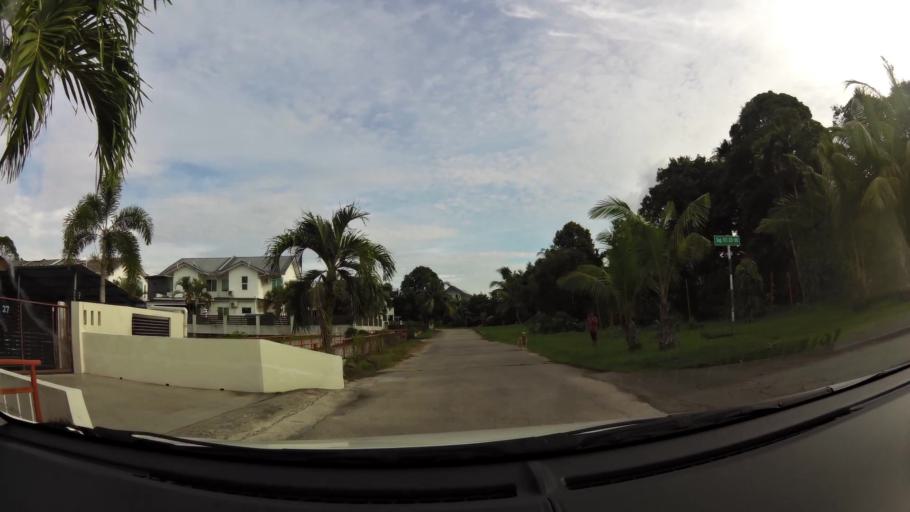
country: BN
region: Brunei and Muara
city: Bandar Seri Begawan
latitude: 4.9014
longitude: 114.8942
